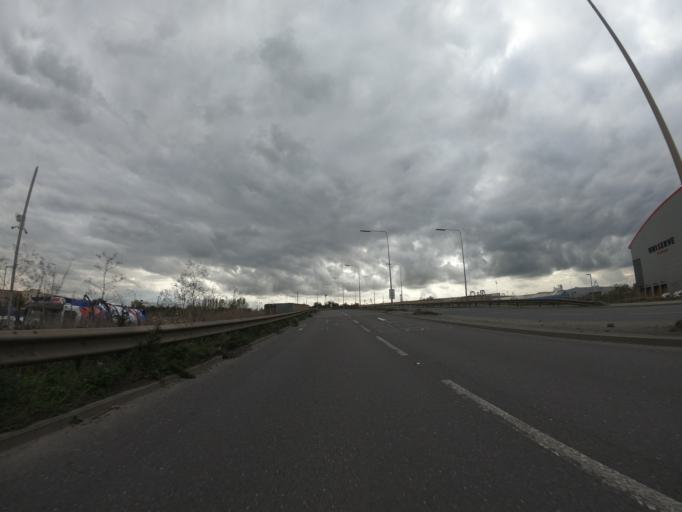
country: GB
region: England
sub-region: Borough of Thurrock
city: Tilbury
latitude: 51.4669
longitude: 0.3480
